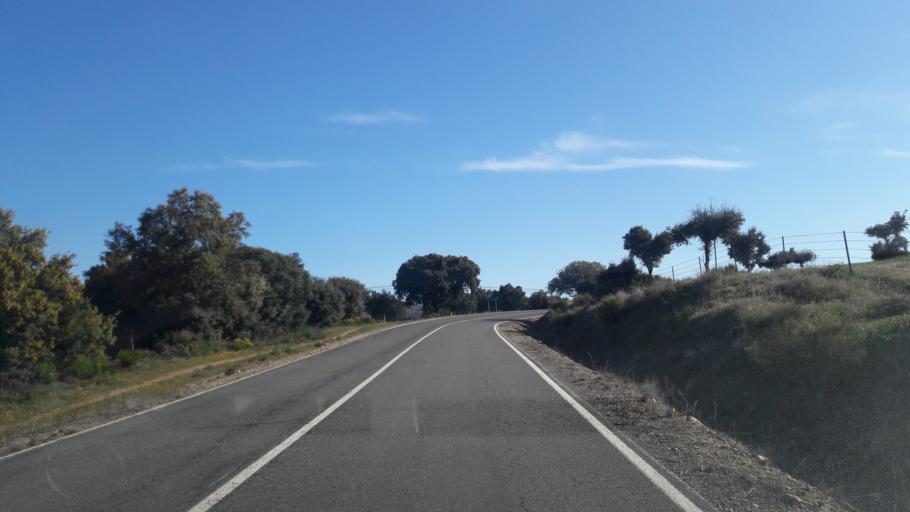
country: ES
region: Castille and Leon
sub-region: Provincia de Avila
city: Narrillos del Alamo
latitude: 40.5301
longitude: -5.4788
